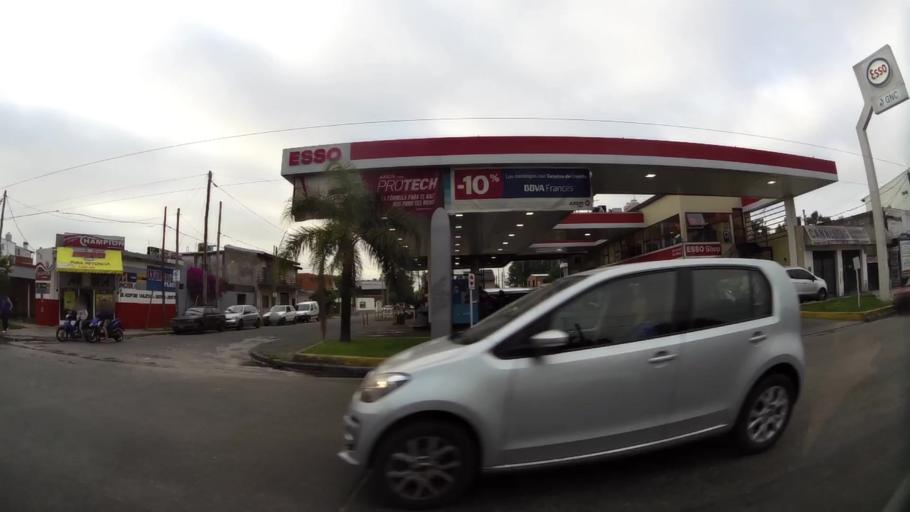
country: AR
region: Buenos Aires
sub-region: Partido de Moron
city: Moron
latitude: -34.6621
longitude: -58.5962
